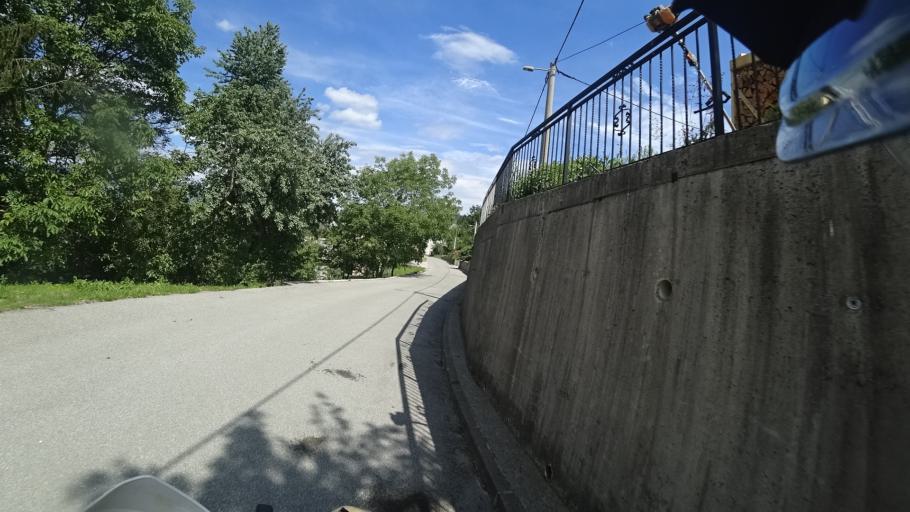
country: SI
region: Osilnica
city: Osilnica
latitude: 45.5144
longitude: 14.6729
